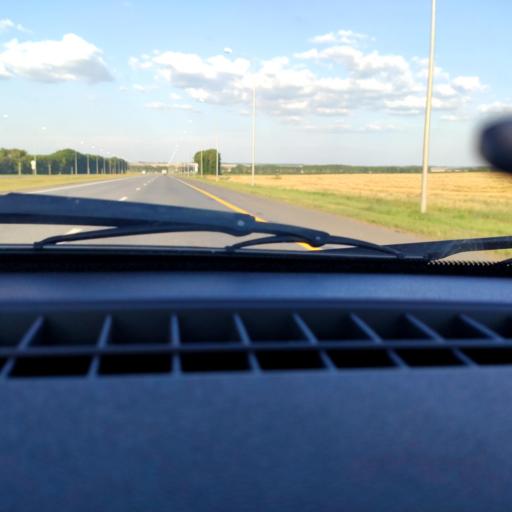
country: RU
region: Bashkortostan
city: Alekseyevka
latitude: 54.7267
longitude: 54.9408
